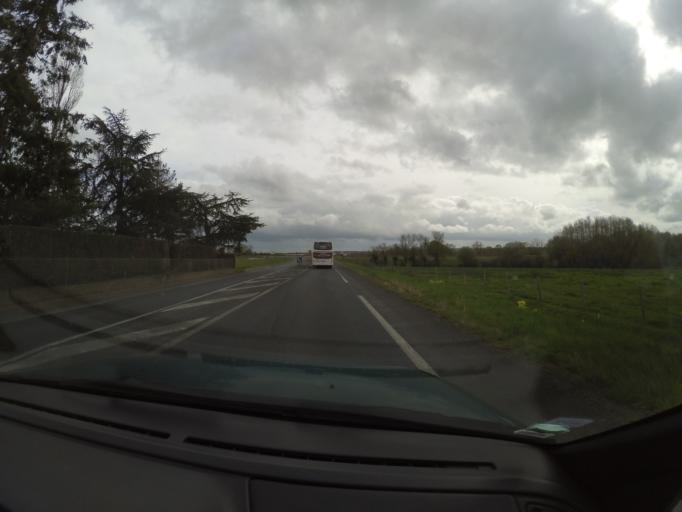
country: FR
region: Pays de la Loire
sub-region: Departement de Maine-et-Loire
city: Lire
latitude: 47.3138
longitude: -1.1626
